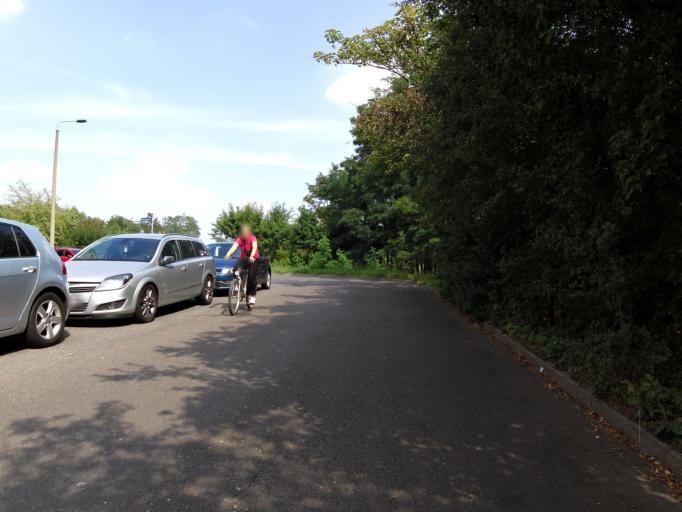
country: DE
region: Saxony
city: Leipzig
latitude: 51.3706
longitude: 12.3492
